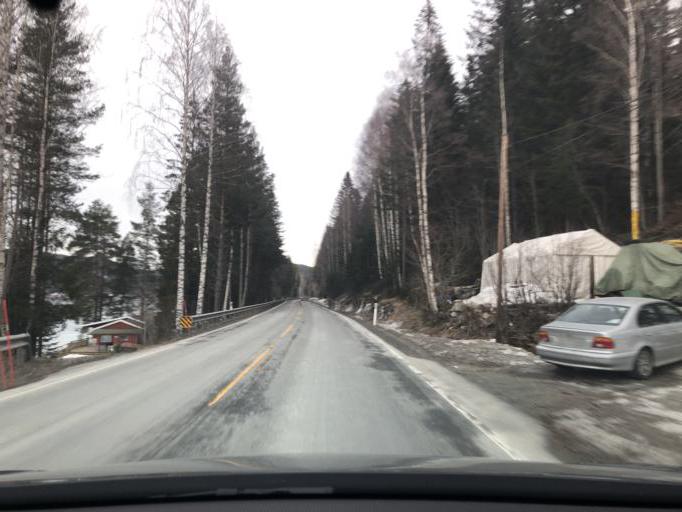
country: NO
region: Buskerud
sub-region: Ringerike
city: Honefoss
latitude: 60.4176
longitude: 10.0891
